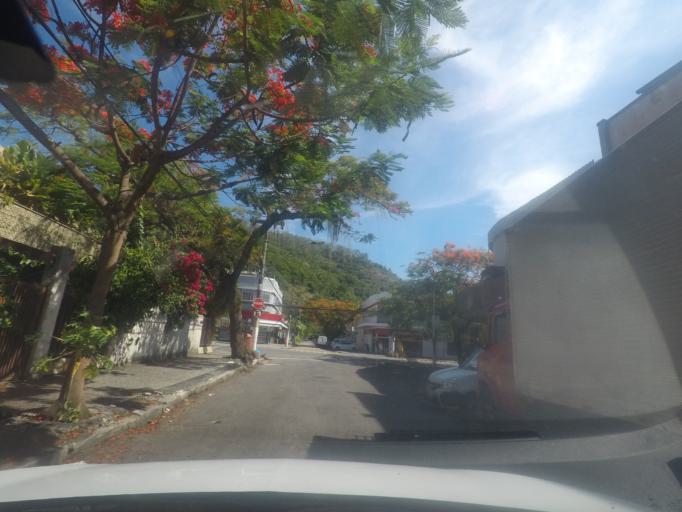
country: BR
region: Rio de Janeiro
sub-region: Niteroi
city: Niteroi
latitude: -22.9198
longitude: -43.0904
